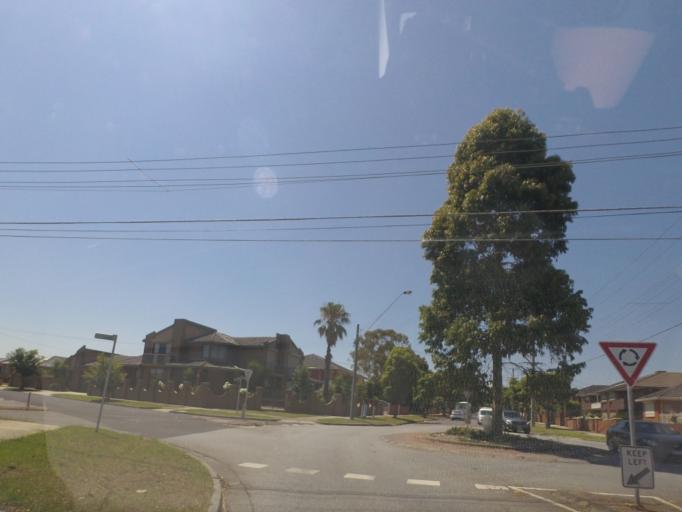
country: AU
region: Victoria
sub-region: Darebin
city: Reservoir
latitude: -37.7021
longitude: 144.9896
